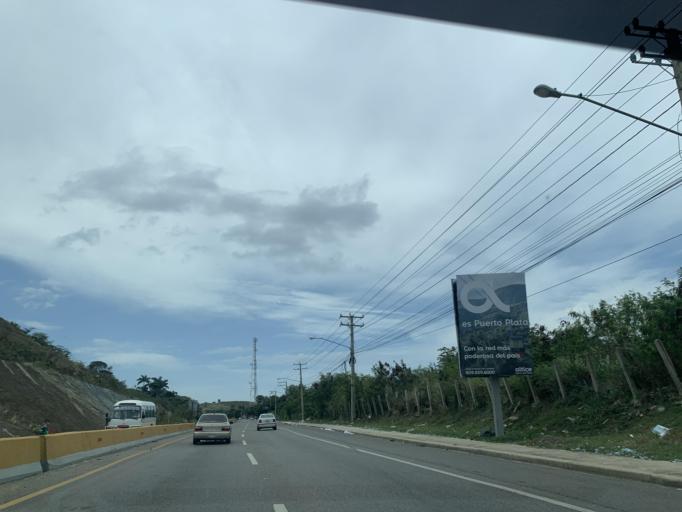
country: DO
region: Puerto Plata
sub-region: Puerto Plata
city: Puerto Plata
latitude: 19.8247
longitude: -70.7455
